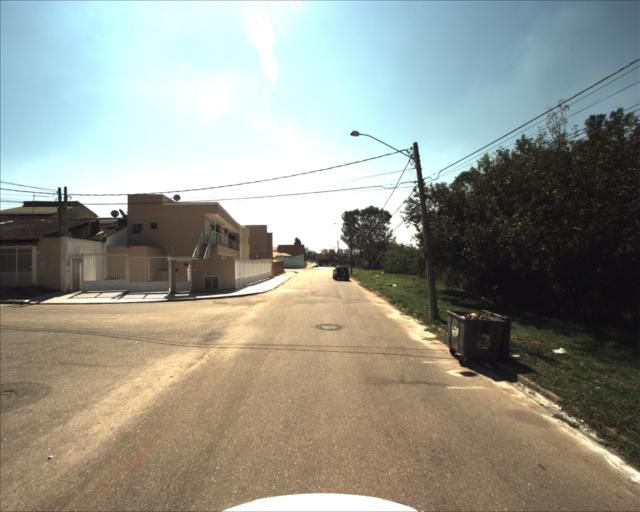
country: BR
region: Sao Paulo
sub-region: Sorocaba
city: Sorocaba
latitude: -23.5097
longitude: -47.5105
